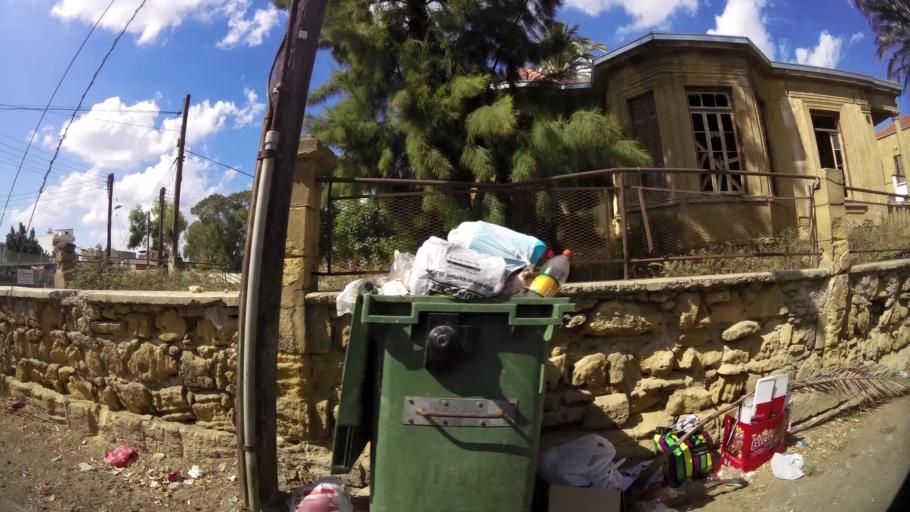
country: CY
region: Lefkosia
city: Nicosia
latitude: 35.1802
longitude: 33.3704
